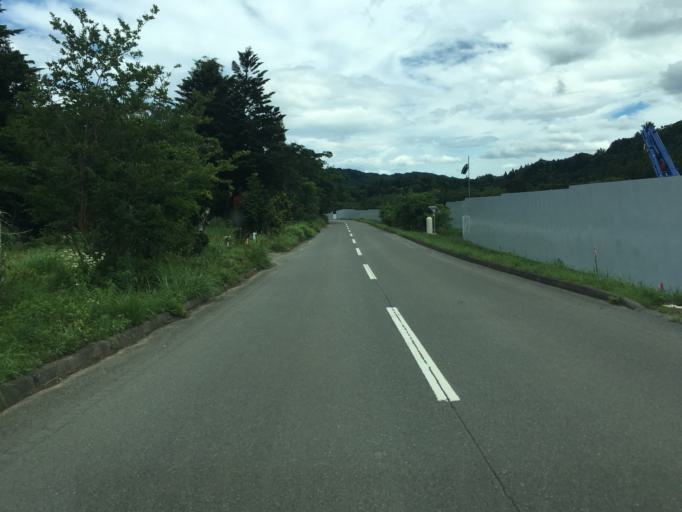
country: JP
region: Fukushima
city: Namie
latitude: 37.6959
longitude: 140.8807
